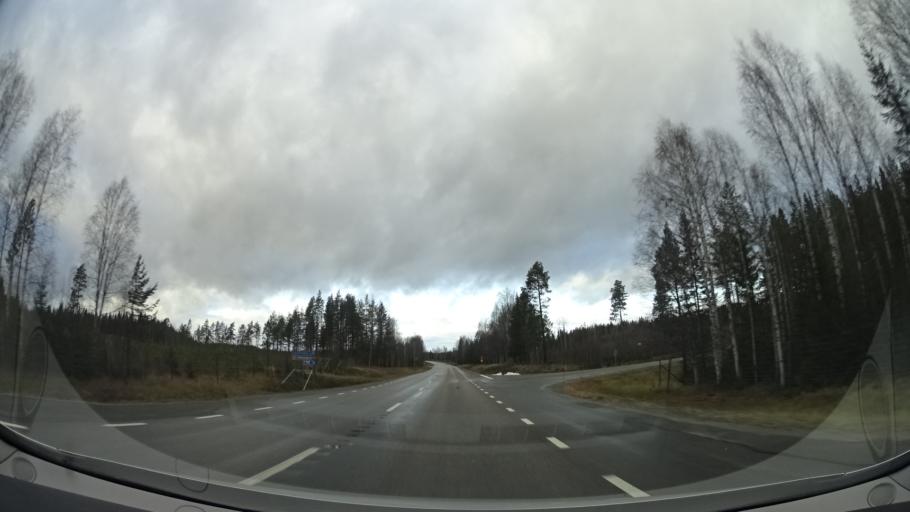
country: SE
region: Vaesterbotten
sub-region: Skelleftea Kommun
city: Viken
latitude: 64.7965
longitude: 20.7422
